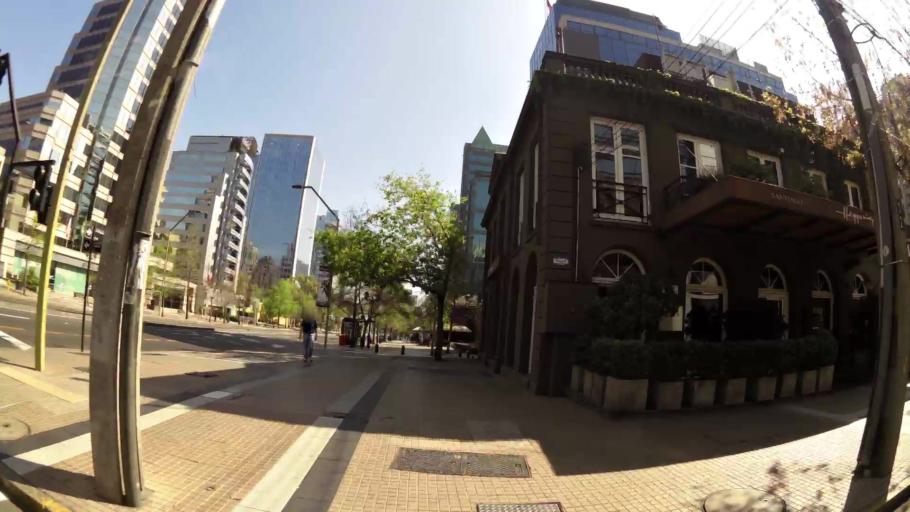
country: CL
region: Santiago Metropolitan
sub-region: Provincia de Santiago
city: Villa Presidente Frei, Nunoa, Santiago, Chile
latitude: -33.4170
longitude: -70.5975
